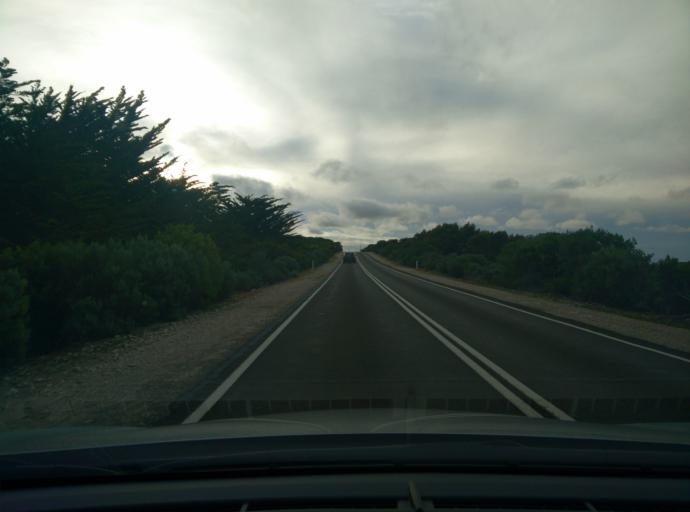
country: AU
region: South Australia
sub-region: Kangaroo Island
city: Kingscote
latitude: -35.8357
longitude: 137.7935
